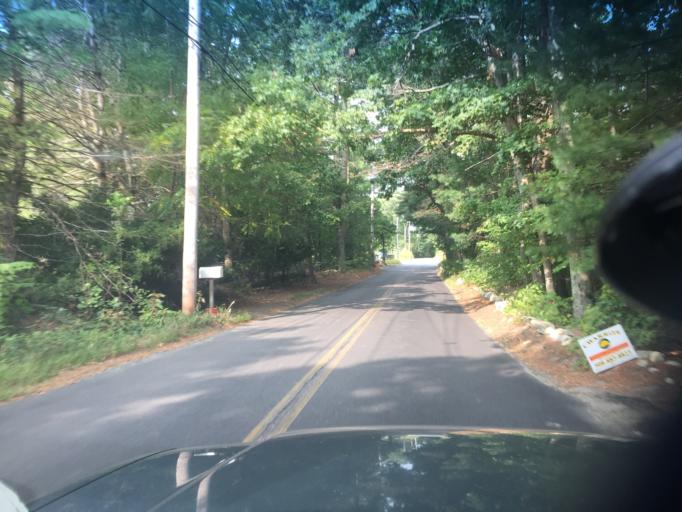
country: US
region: Massachusetts
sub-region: Norfolk County
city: Bellingham
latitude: 42.1310
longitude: -71.4535
